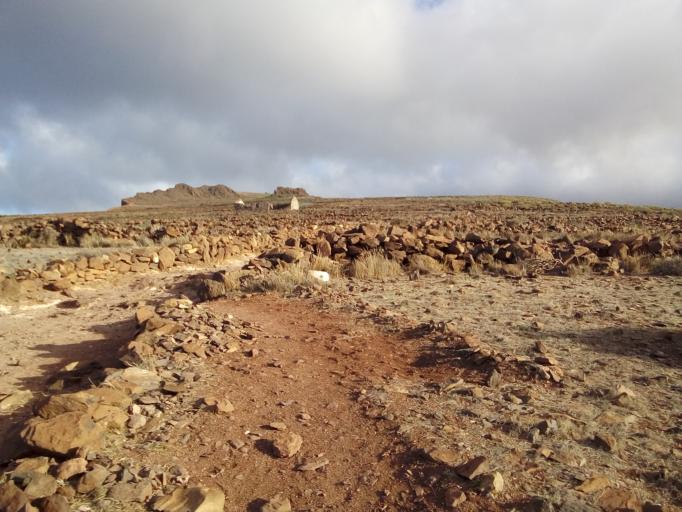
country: ES
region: Canary Islands
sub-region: Provincia de Santa Cruz de Tenerife
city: Vallehermosa
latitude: 28.1062
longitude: -17.3370
